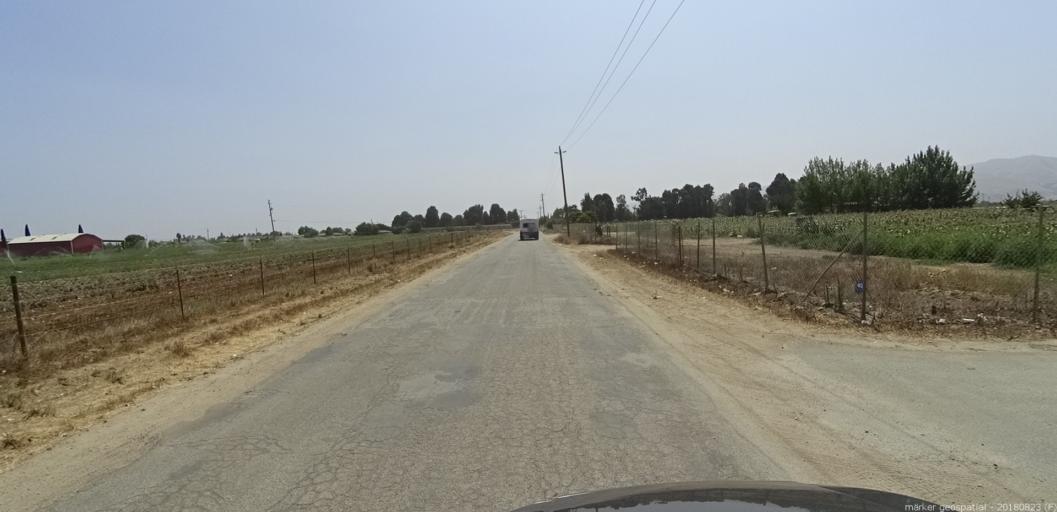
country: US
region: California
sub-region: Monterey County
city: Greenfield
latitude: 36.3182
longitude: -121.2629
